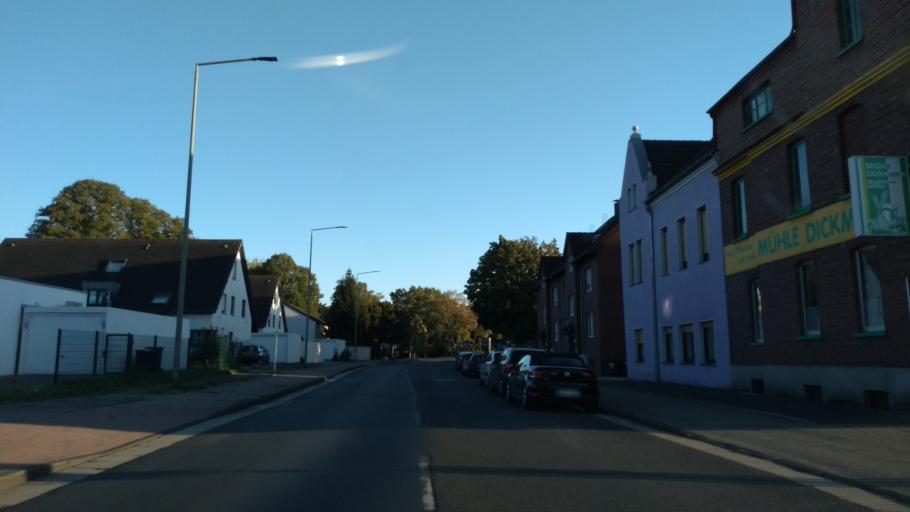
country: DE
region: North Rhine-Westphalia
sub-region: Regierungsbezirk Dusseldorf
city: Dinslaken
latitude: 51.5449
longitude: 6.7152
